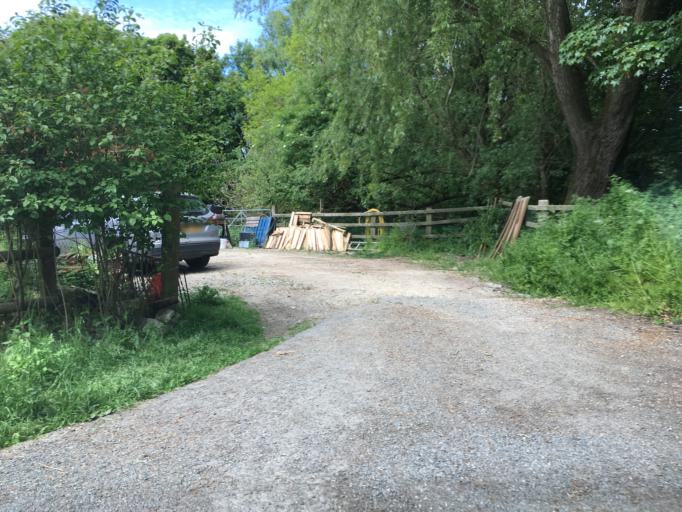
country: GB
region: England
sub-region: South Gloucestershire
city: Charfield
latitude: 51.6708
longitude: -2.4060
